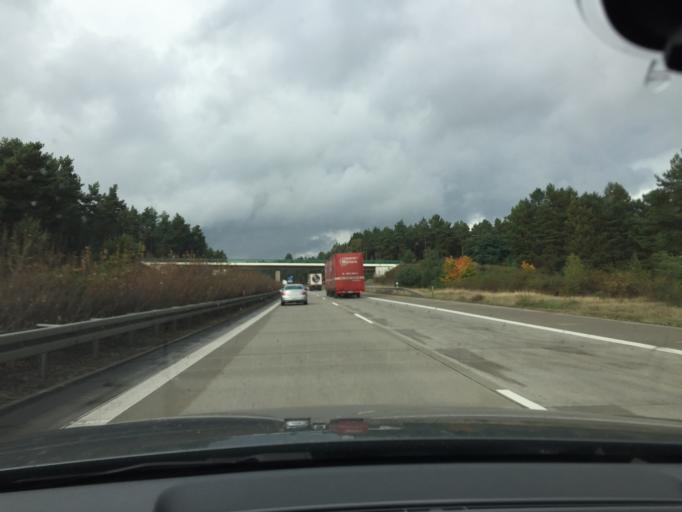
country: DE
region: Brandenburg
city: Schwerin
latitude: 52.1944
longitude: 13.6155
